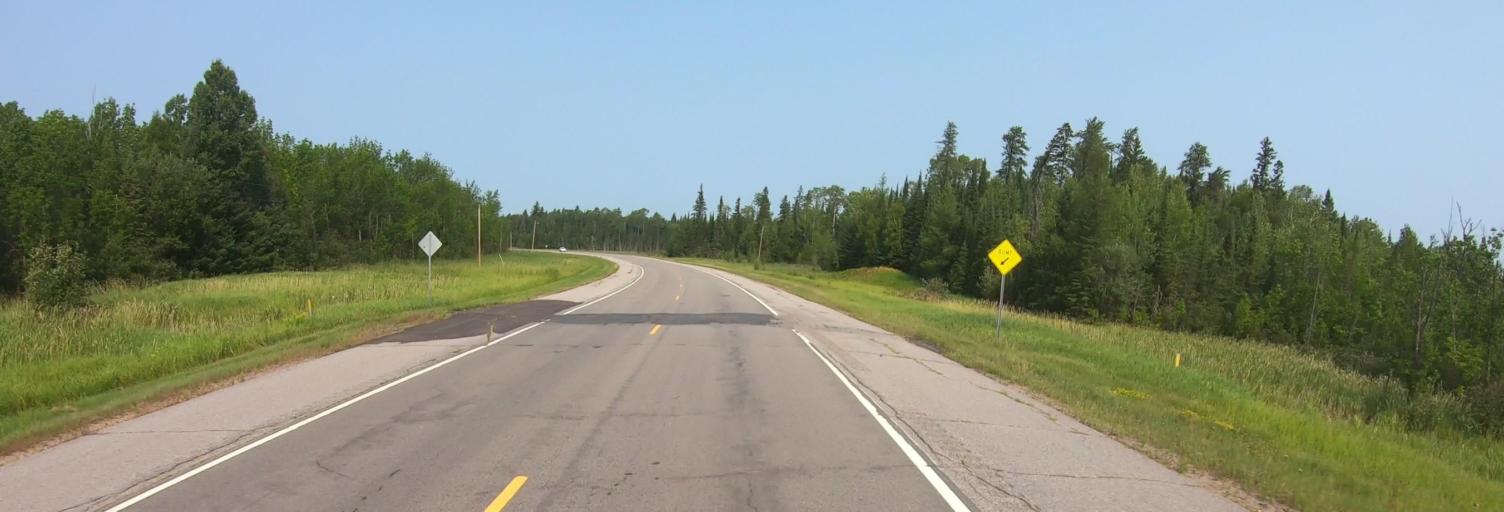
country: US
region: Minnesota
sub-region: Saint Louis County
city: Mountain Iron
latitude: 48.0878
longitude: -92.8230
